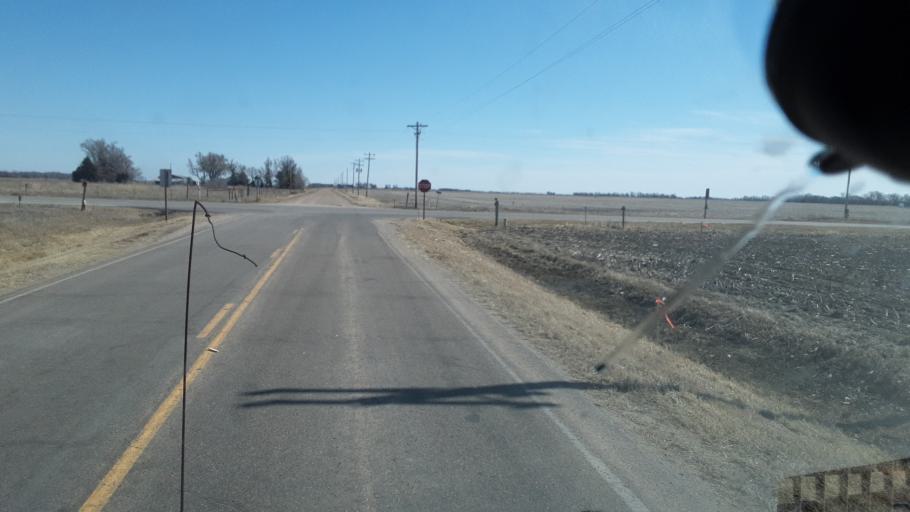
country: US
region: Kansas
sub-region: Rice County
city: Sterling
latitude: 38.2463
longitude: -98.2075
